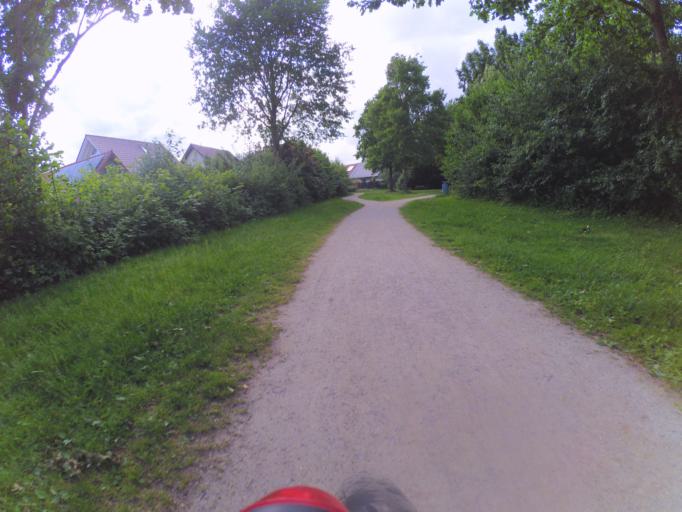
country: DE
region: North Rhine-Westphalia
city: Ibbenburen
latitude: 52.2808
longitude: 7.6991
